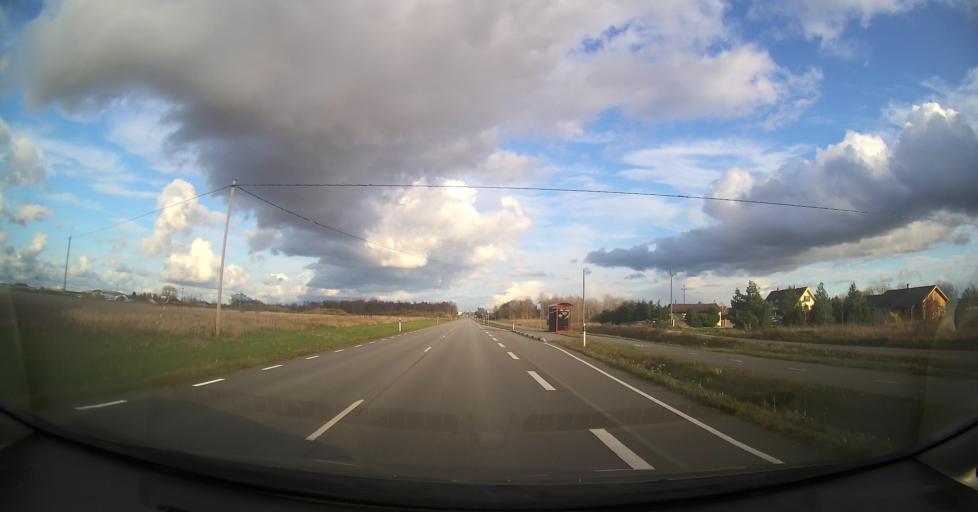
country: EE
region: Harju
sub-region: Joelaehtme vald
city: Loo
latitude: 59.4476
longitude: 24.9611
